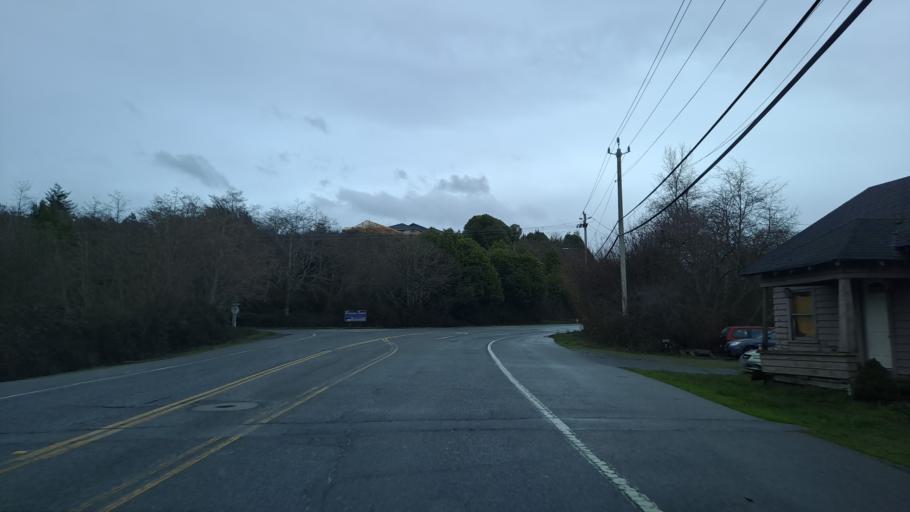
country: US
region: California
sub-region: Humboldt County
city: Fortuna
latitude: 40.5894
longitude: -124.1339
